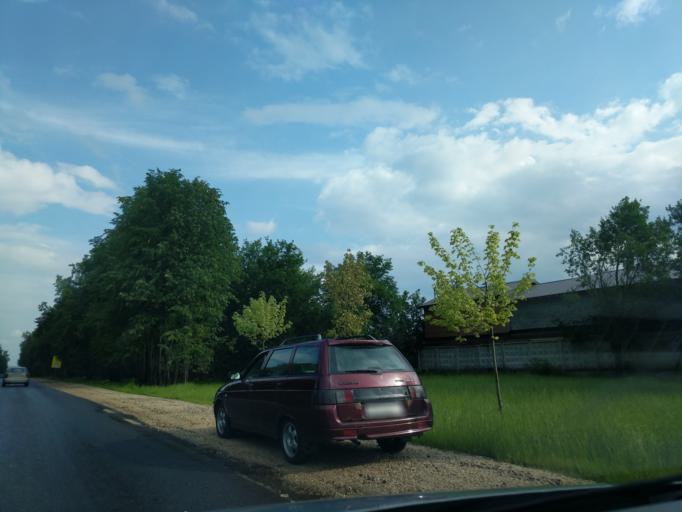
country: RU
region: Moskovskaya
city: Lobnya
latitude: 56.0081
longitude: 37.5104
